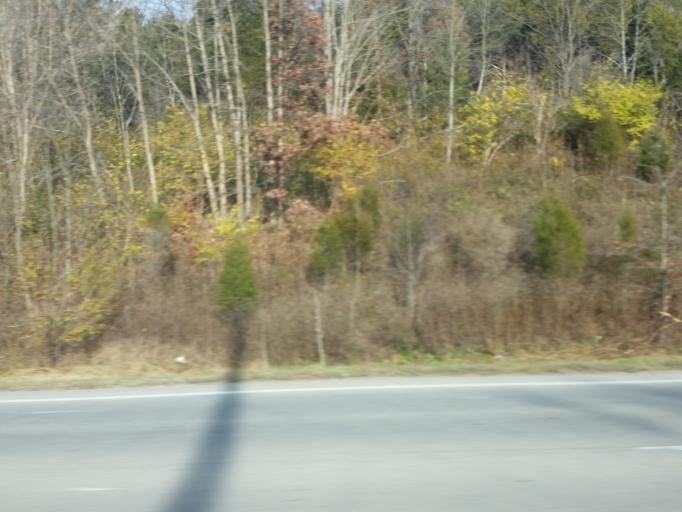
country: US
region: Kentucky
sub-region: Campbell County
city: Claryville
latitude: 38.8225
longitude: -84.3631
